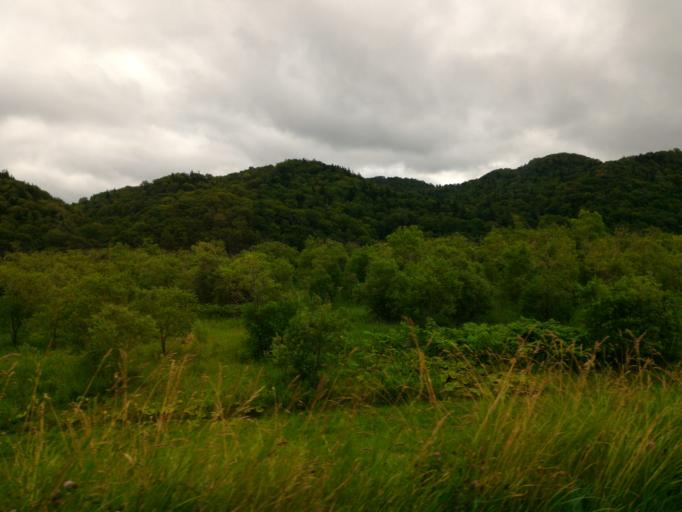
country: JP
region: Hokkaido
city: Nayoro
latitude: 44.7958
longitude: 142.0676
